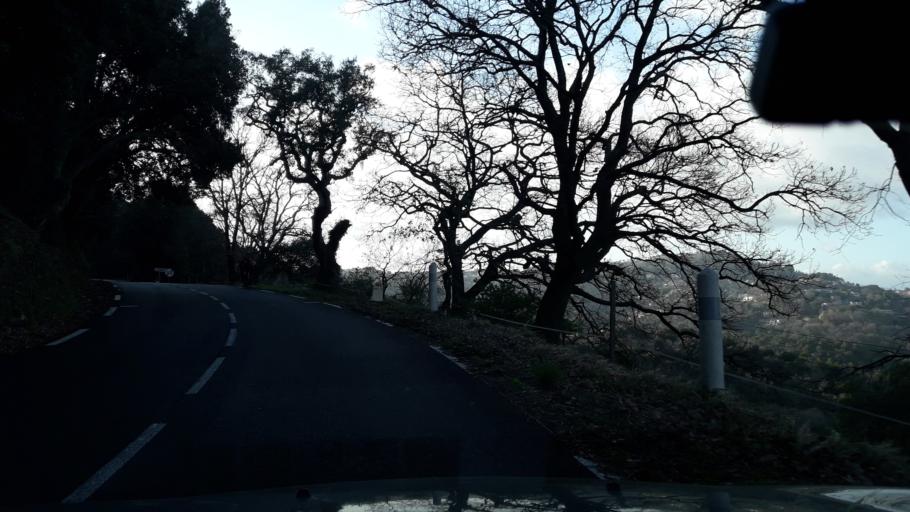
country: FR
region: Provence-Alpes-Cote d'Azur
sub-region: Departement du Var
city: Tanneron
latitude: 43.5152
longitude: 6.8253
